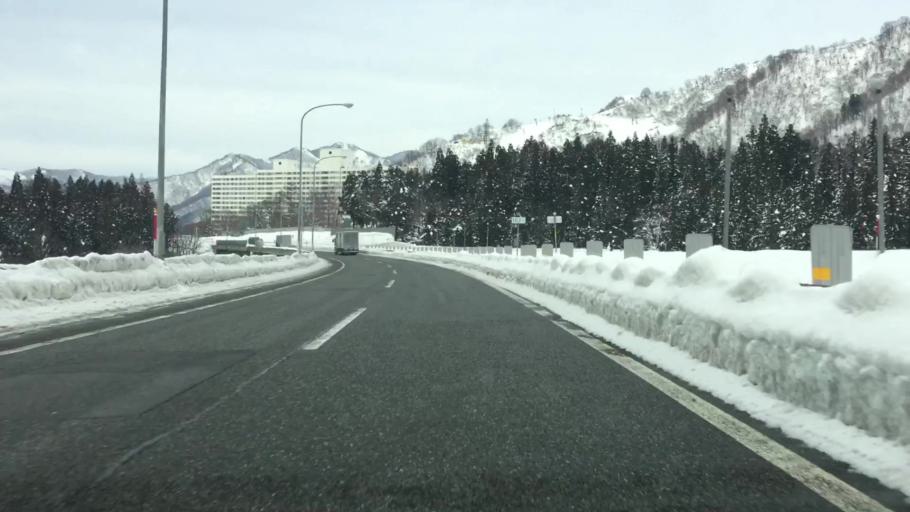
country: JP
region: Niigata
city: Shiozawa
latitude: 36.9000
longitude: 138.8470
